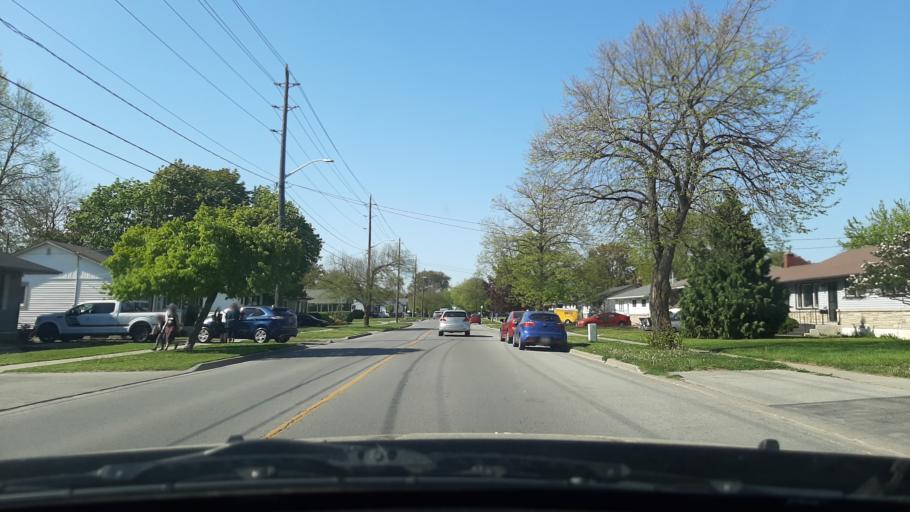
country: CA
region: Ontario
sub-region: Regional Municipality of Niagara
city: St. Catharines
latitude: 43.2020
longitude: -79.2114
